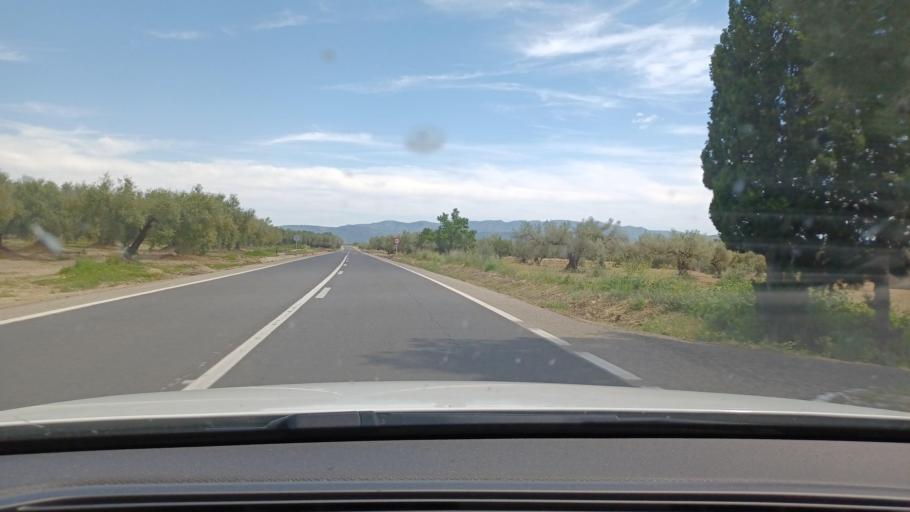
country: ES
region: Catalonia
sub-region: Provincia de Tarragona
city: Mas de Barberans
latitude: 40.6413
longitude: 0.3594
